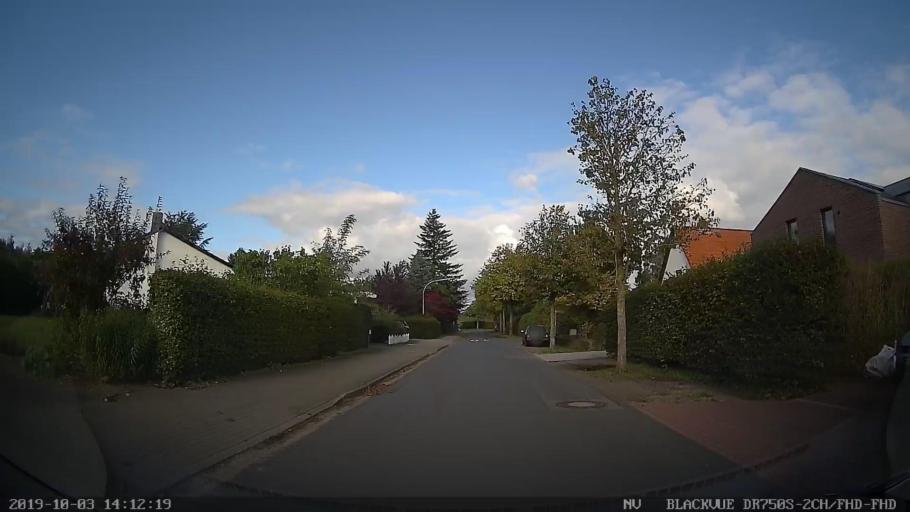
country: DE
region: Schleswig-Holstein
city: Rellingen
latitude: 53.6610
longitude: 9.8313
